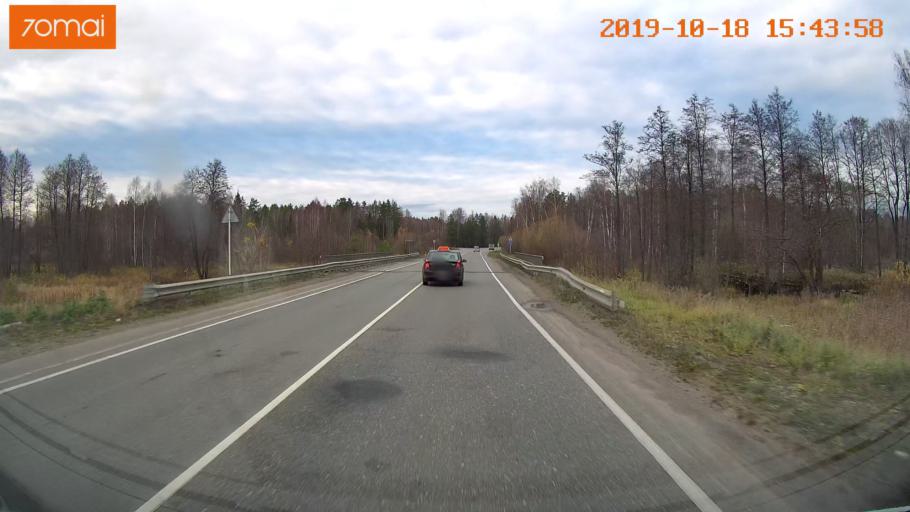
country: RU
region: Vladimir
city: Golovino
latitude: 55.9753
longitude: 40.5474
